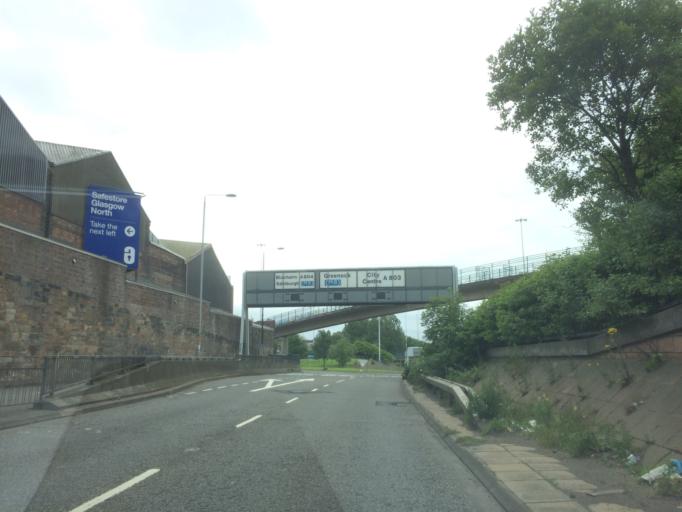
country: GB
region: Scotland
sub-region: Glasgow City
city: Glasgow
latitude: 55.8709
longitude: -4.2338
